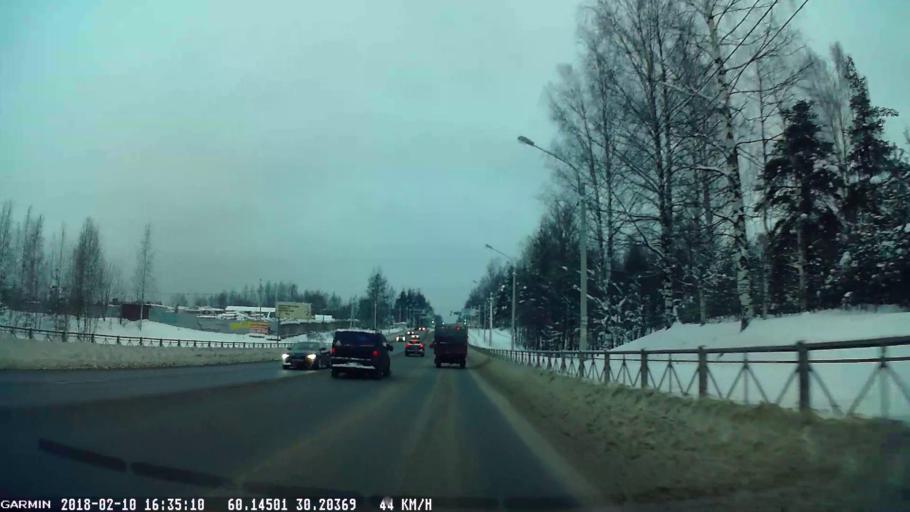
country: RU
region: Leningrad
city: Sertolovo
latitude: 60.1457
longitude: 30.2028
